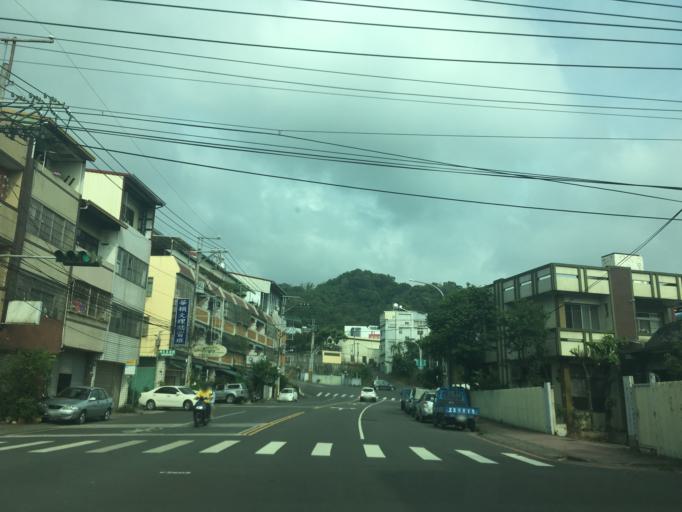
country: TW
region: Taiwan
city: Fengyuan
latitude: 24.2419
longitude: 120.7322
